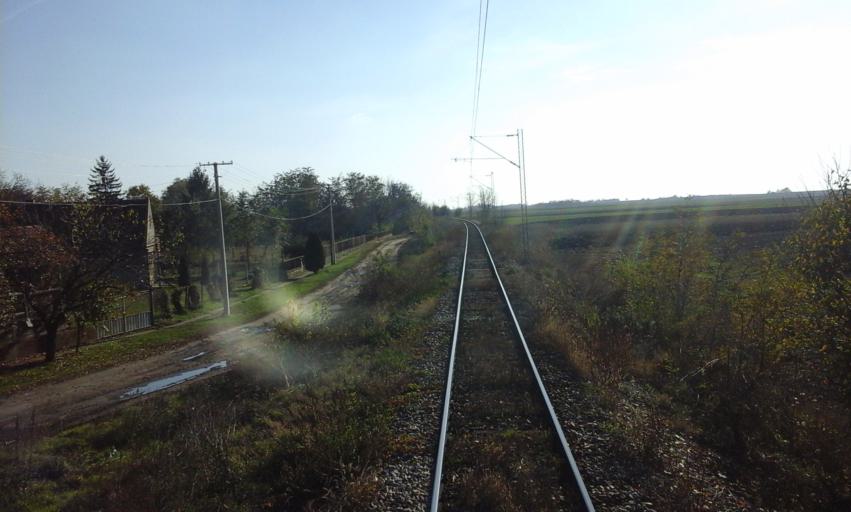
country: RS
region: Autonomna Pokrajina Vojvodina
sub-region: Severnobacki Okrug
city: Backa Topola
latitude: 45.8044
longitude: 19.6475
